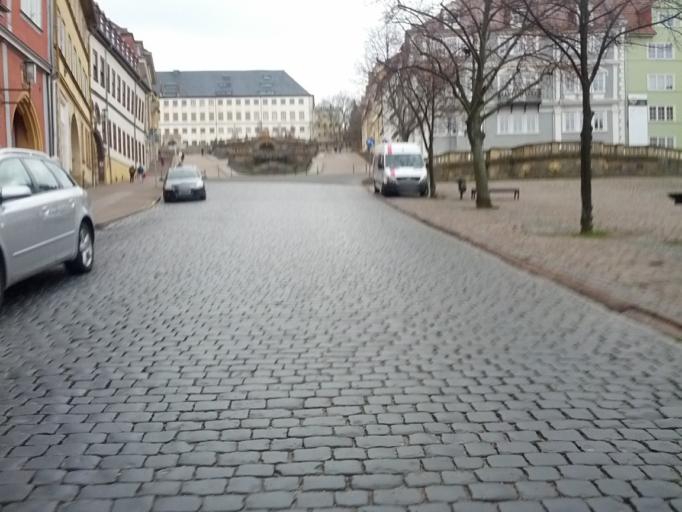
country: DE
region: Thuringia
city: Gotha
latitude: 50.9482
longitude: 10.7022
